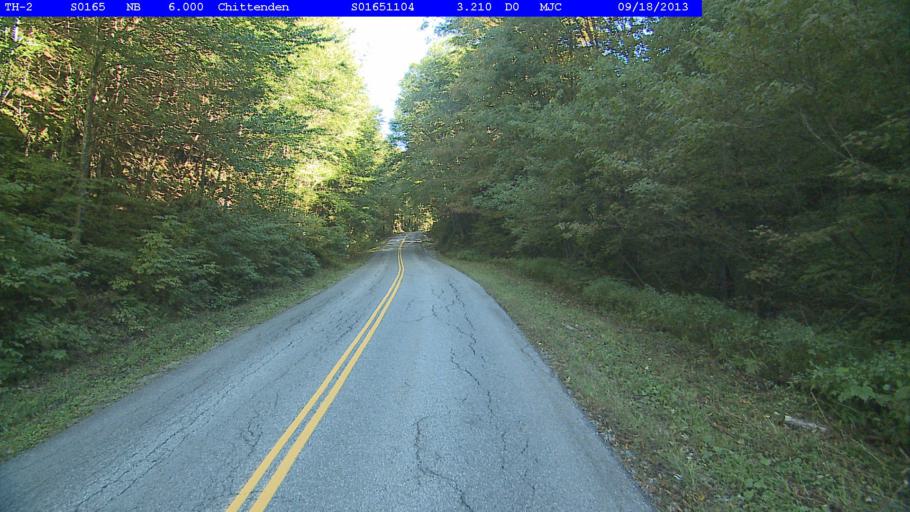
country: US
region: Vermont
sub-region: Rutland County
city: Rutland
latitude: 43.7210
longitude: -72.9660
